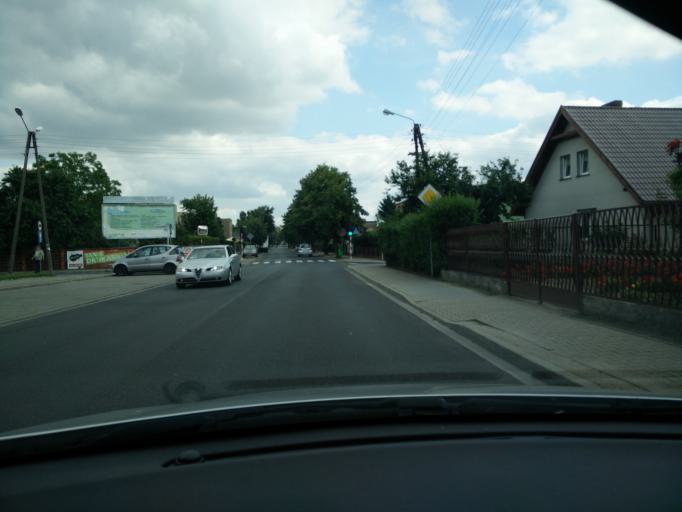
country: PL
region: Greater Poland Voivodeship
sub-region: Powiat sredzki
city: Sroda Wielkopolska
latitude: 52.2304
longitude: 17.2615
